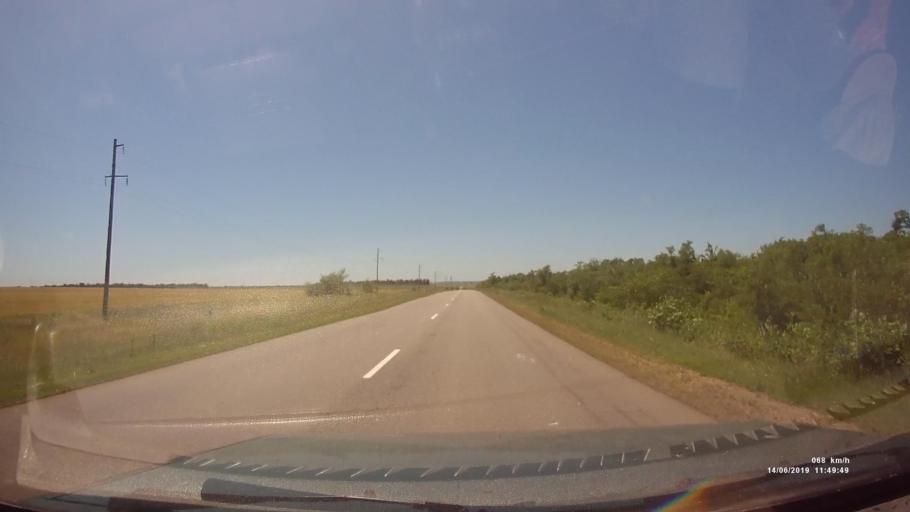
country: RU
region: Rostov
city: Kazanskaya
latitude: 49.8517
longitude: 41.2734
